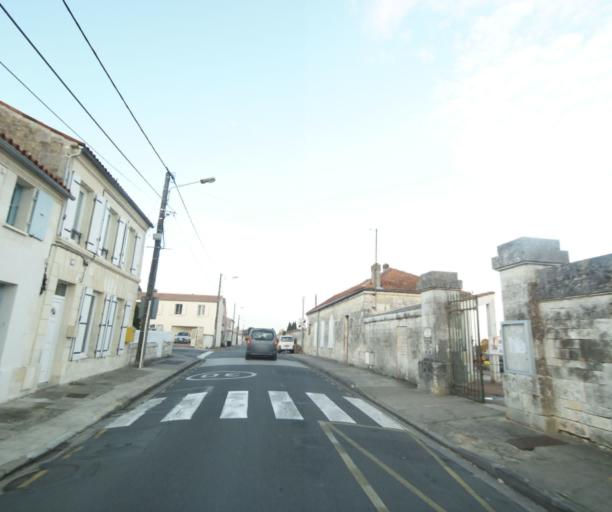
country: FR
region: Poitou-Charentes
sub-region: Departement de la Charente-Maritime
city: Saintes
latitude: 45.7514
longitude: -0.6388
